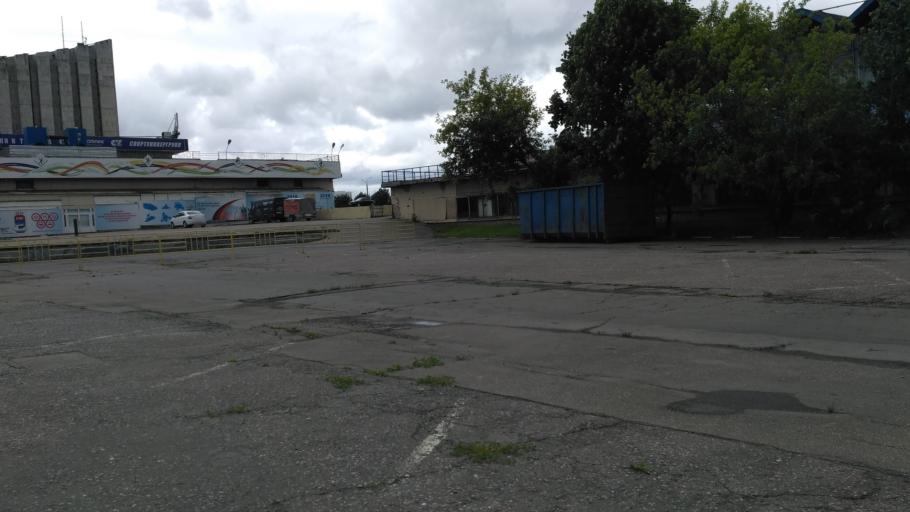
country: RU
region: Moscow
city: Metrogorodok
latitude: 55.8011
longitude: 37.7586
